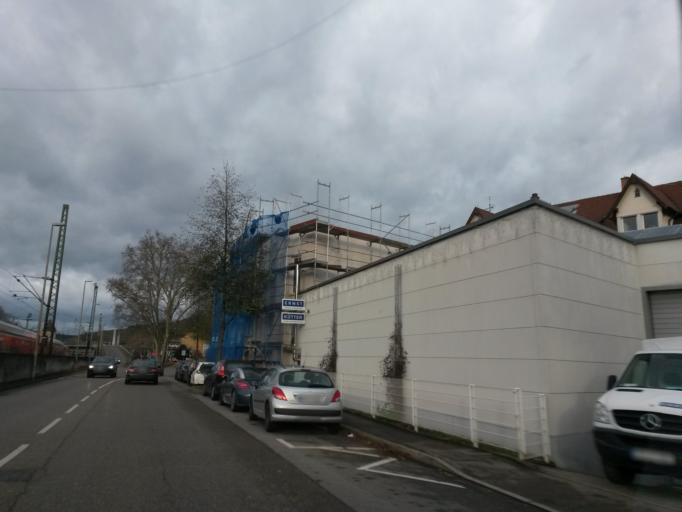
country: DE
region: Baden-Wuerttemberg
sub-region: Regierungsbezirk Stuttgart
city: Esslingen
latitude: 48.7357
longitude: 9.3104
